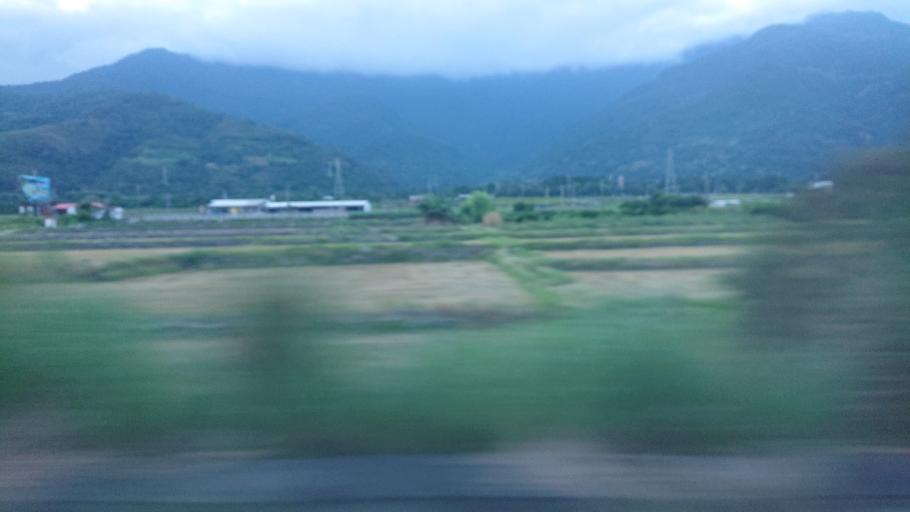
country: TW
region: Taiwan
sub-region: Taitung
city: Taitung
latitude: 23.0361
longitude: 121.1614
